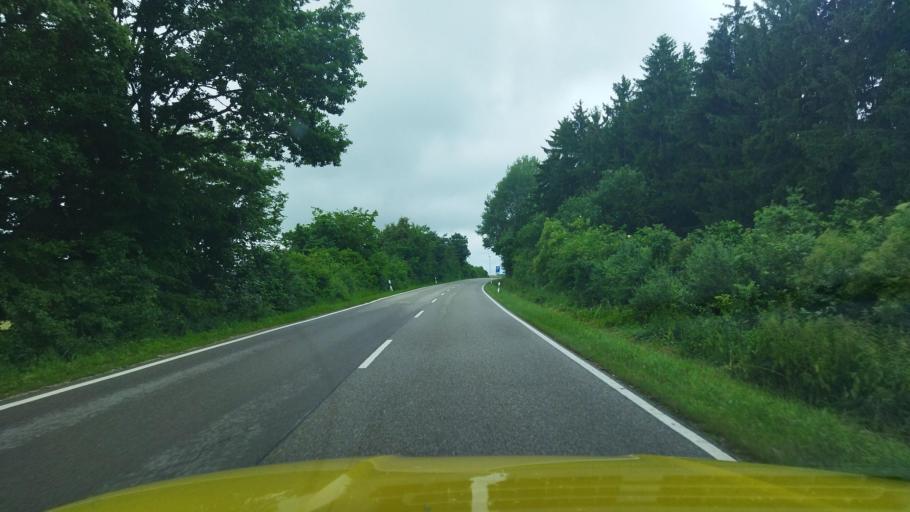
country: DE
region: Bavaria
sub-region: Upper Bavaria
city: Denkendorf
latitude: 48.9442
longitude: 11.5481
